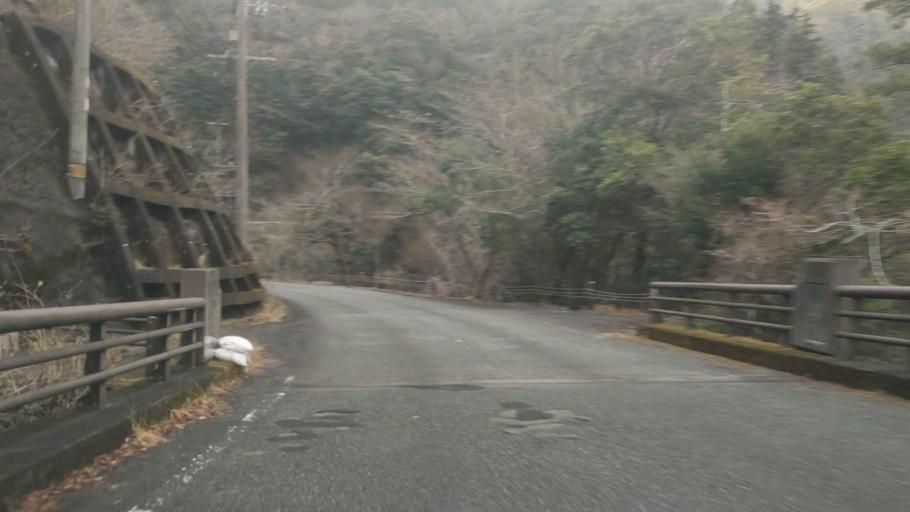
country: JP
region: Kumamoto
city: Matsubase
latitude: 32.5094
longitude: 130.9226
